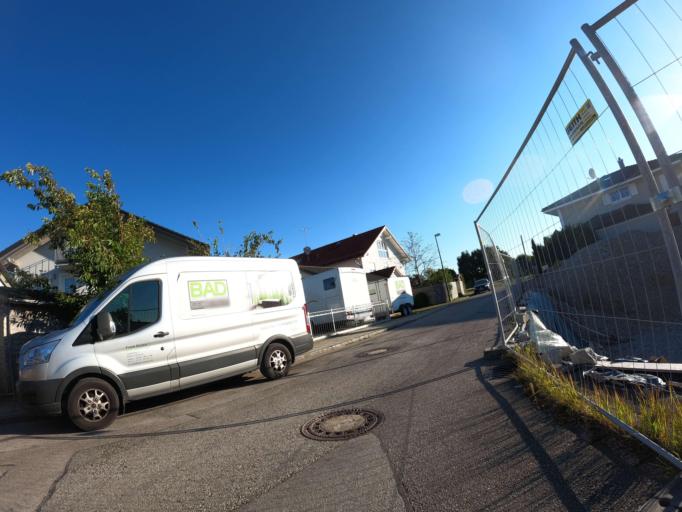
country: DE
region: Bavaria
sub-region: Upper Bavaria
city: Grasbrunn
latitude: 48.0575
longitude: 11.7763
